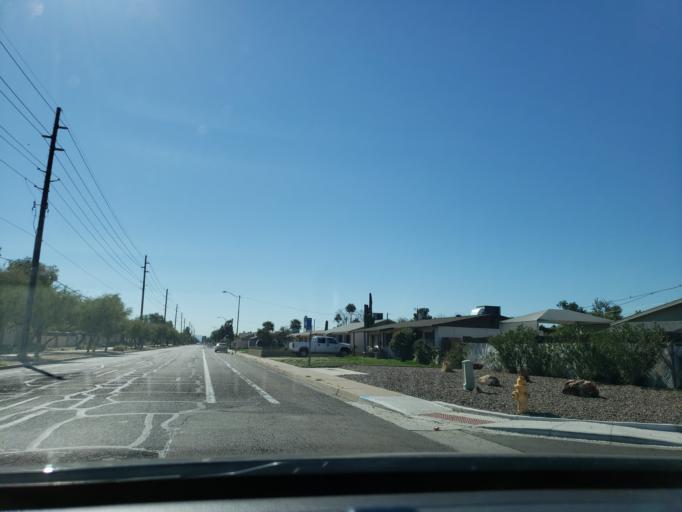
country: US
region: Arizona
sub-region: Maricopa County
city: Glendale
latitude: 33.6070
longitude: -112.1253
